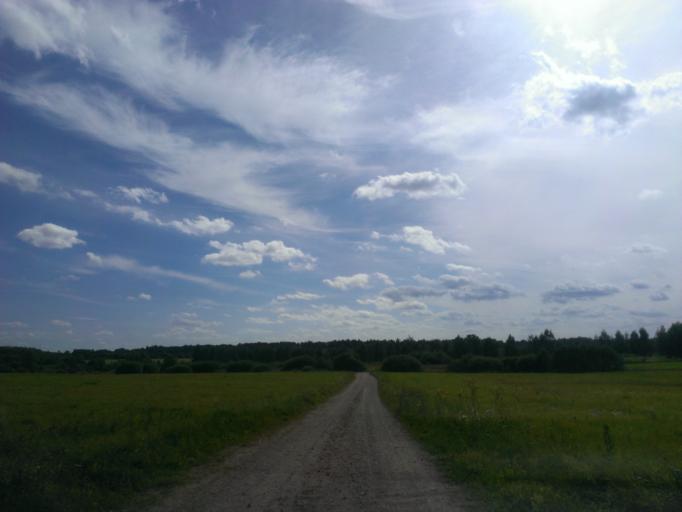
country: LV
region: Ligatne
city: Ligatne
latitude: 57.2230
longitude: 25.0070
